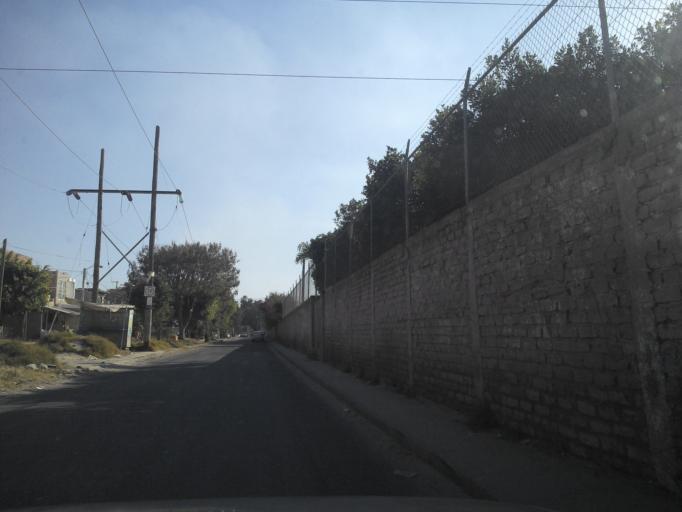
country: MX
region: Jalisco
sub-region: San Pedro Tlaquepaque
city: Paseo del Prado
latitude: 20.5930
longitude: -103.3896
